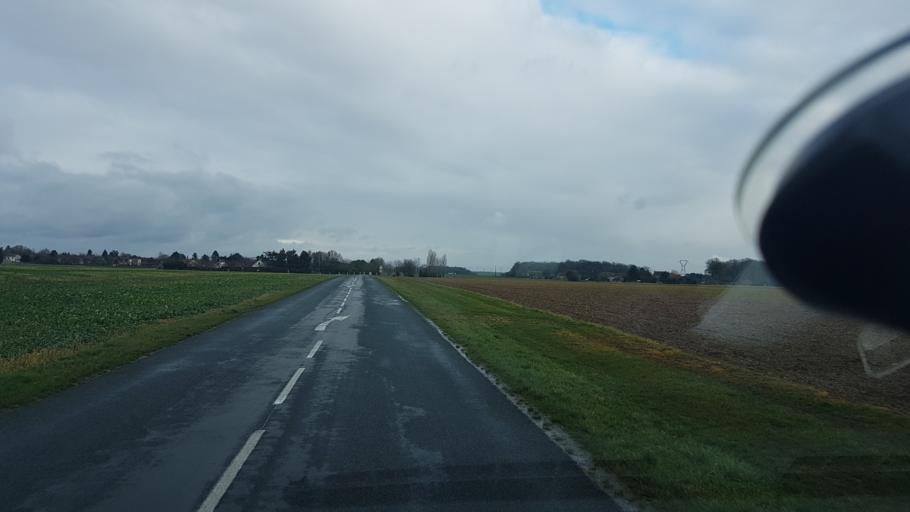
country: FR
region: Ile-de-France
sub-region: Departement de Seine-et-Marne
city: Souppes-sur-Loing
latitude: 48.2002
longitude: 2.7757
